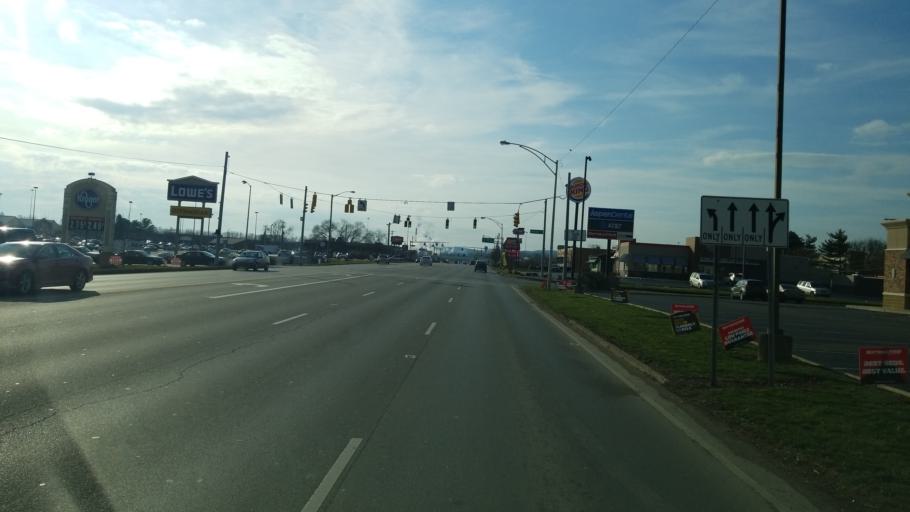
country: US
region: Ohio
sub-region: Ross County
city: Chillicothe
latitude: 39.3544
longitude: -82.9766
